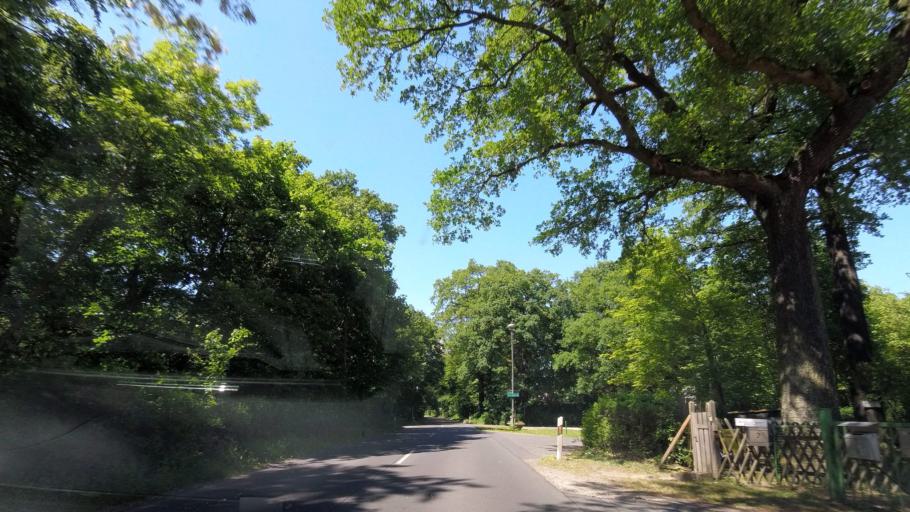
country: DE
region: Brandenburg
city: Potsdam
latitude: 52.3958
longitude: 13.0090
